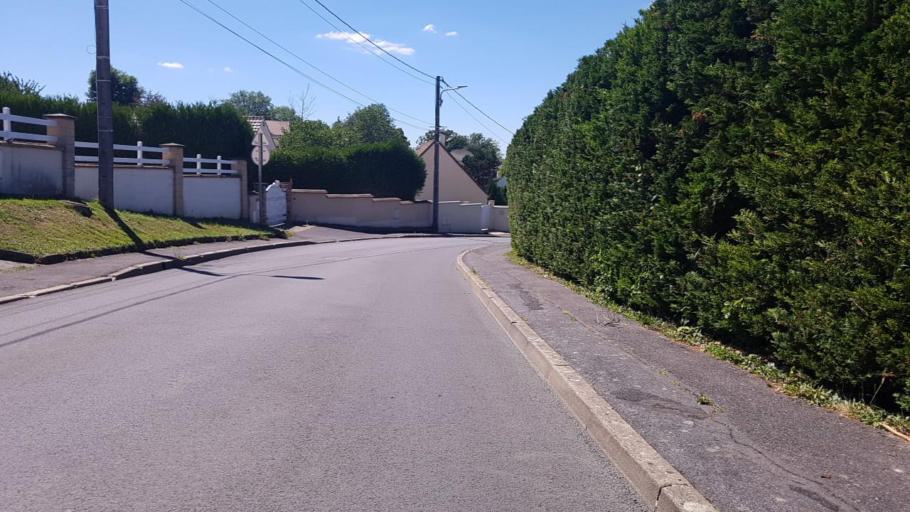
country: FR
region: Ile-de-France
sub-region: Departement de Seine-et-Marne
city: Fublaines
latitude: 48.9393
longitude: 2.9350
